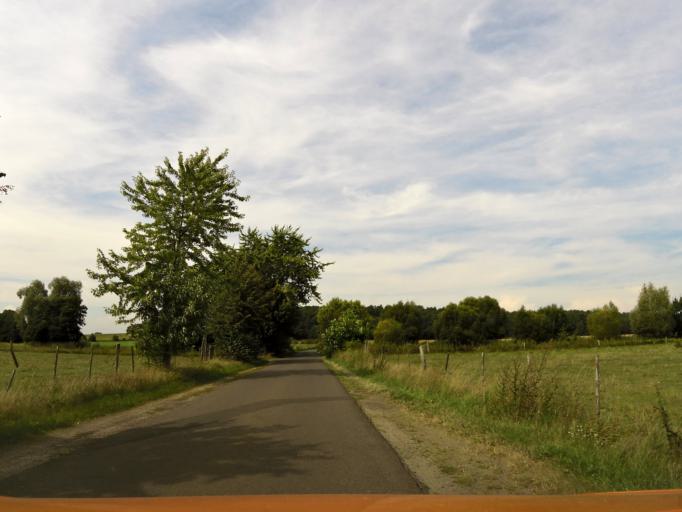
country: DE
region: Brandenburg
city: Michendorf
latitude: 52.2389
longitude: 13.1017
